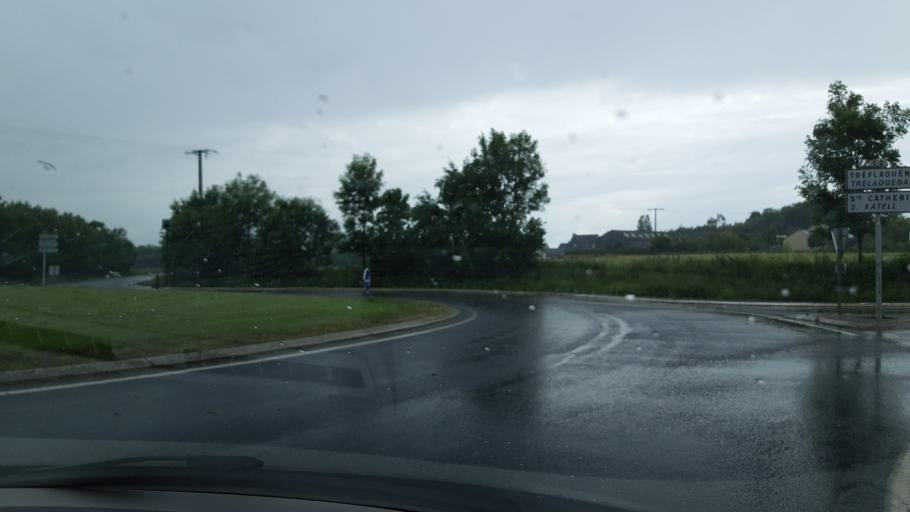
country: FR
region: Brittany
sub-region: Departement du Finistere
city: Plouvorn
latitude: 48.6184
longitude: -4.0549
